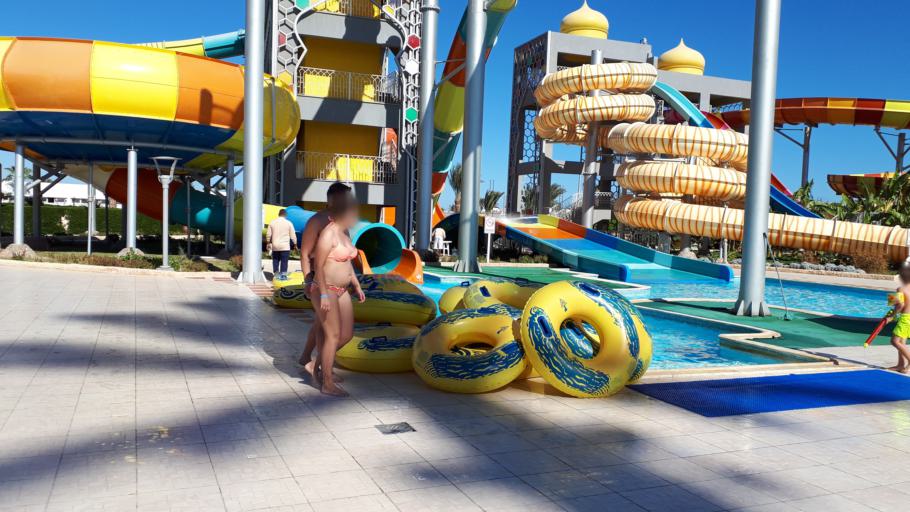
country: EG
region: Red Sea
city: Makadi Bay
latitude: 27.1049
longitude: 33.8263
